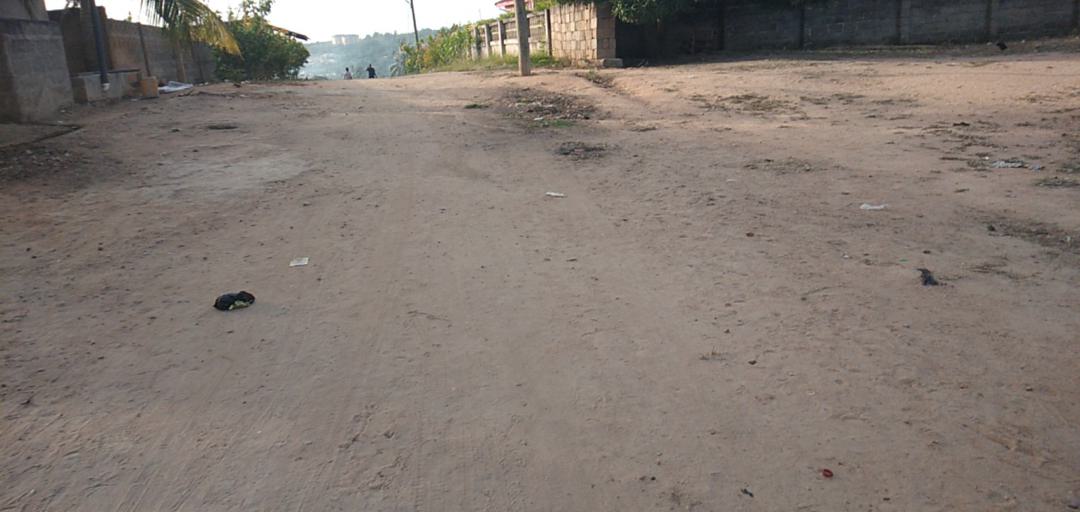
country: GH
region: Central
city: Winneba
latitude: 5.3557
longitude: -0.6142
